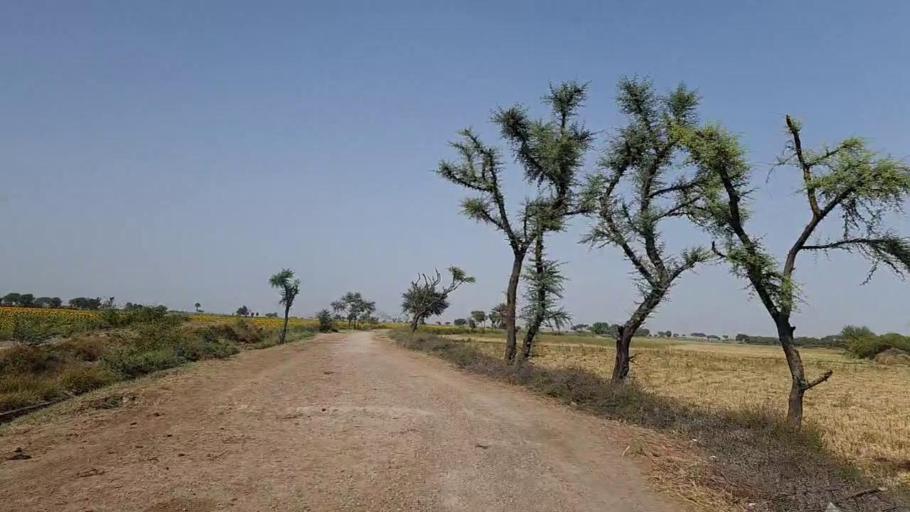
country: PK
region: Sindh
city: Jati
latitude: 24.3432
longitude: 68.3044
